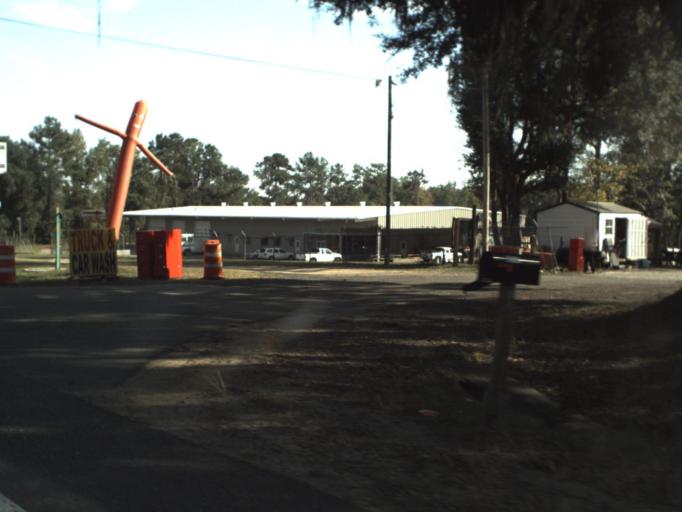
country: US
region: Florida
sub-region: Gadsden County
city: Midway
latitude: 30.4956
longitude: -84.4338
